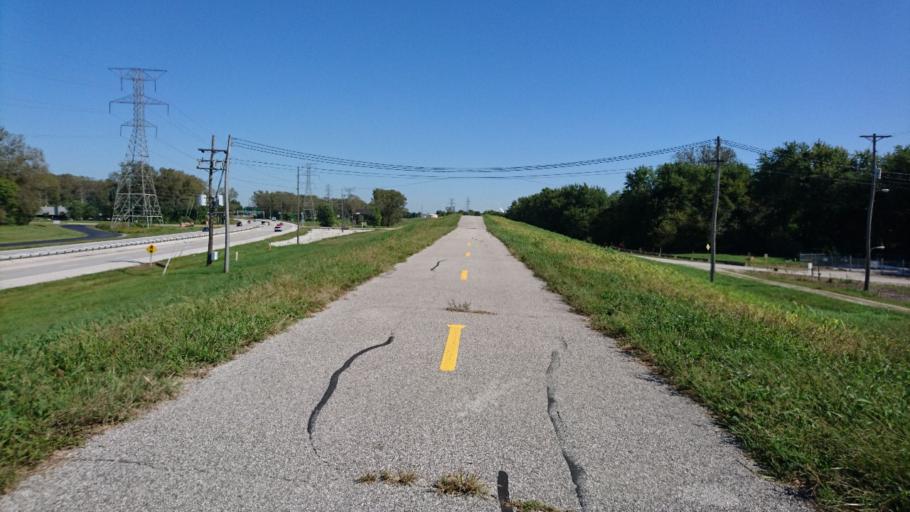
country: US
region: Illinois
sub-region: Madison County
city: Wood River
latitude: 38.8573
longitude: -90.1187
